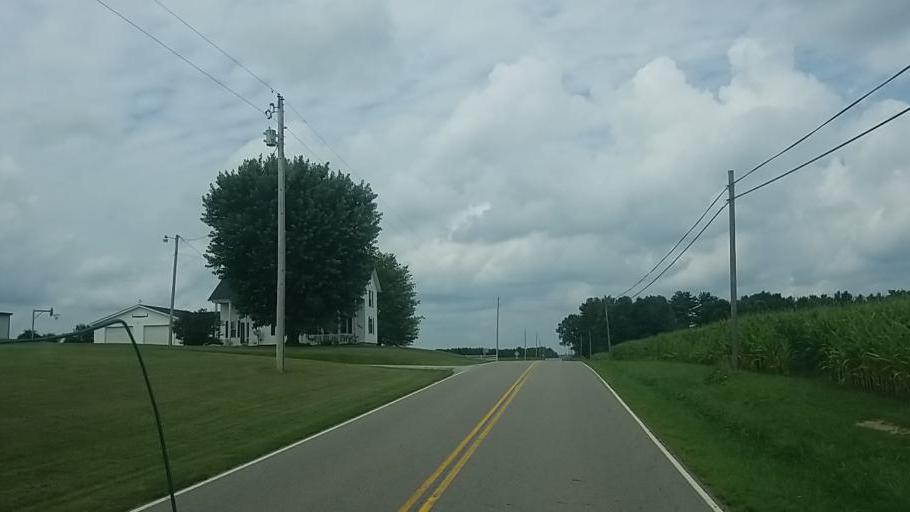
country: US
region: Ohio
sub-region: Licking County
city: Utica
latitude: 40.2138
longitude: -82.3666
